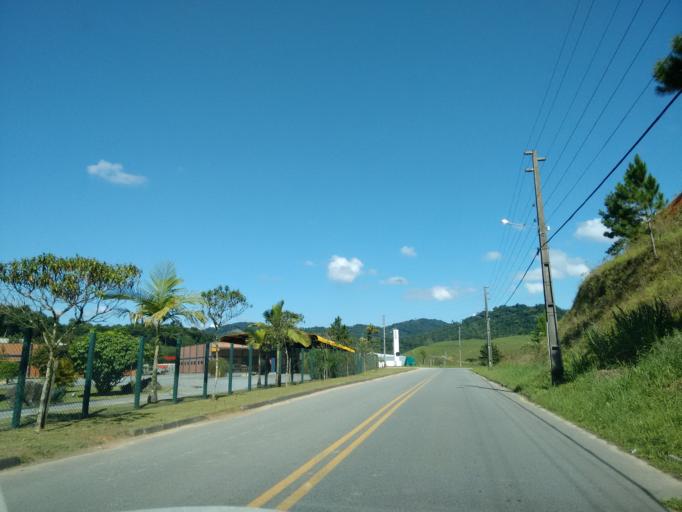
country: BR
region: Santa Catarina
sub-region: Pomerode
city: Pomerode
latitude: -26.8206
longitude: -49.1671
